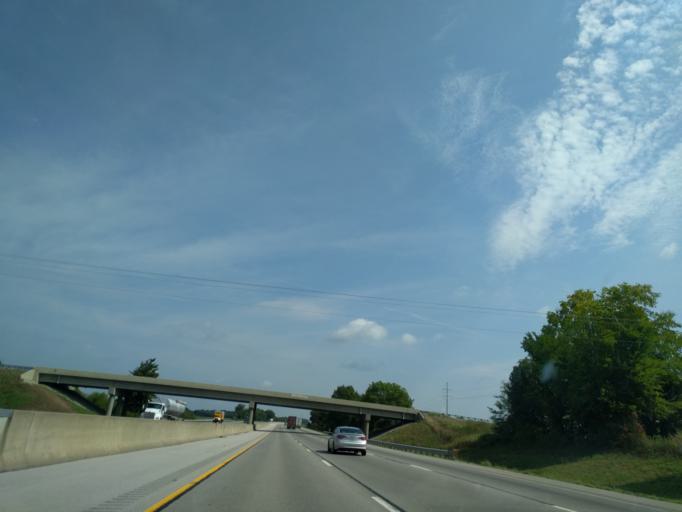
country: US
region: Kentucky
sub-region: Warren County
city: Plano
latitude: 36.8317
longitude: -86.4667
